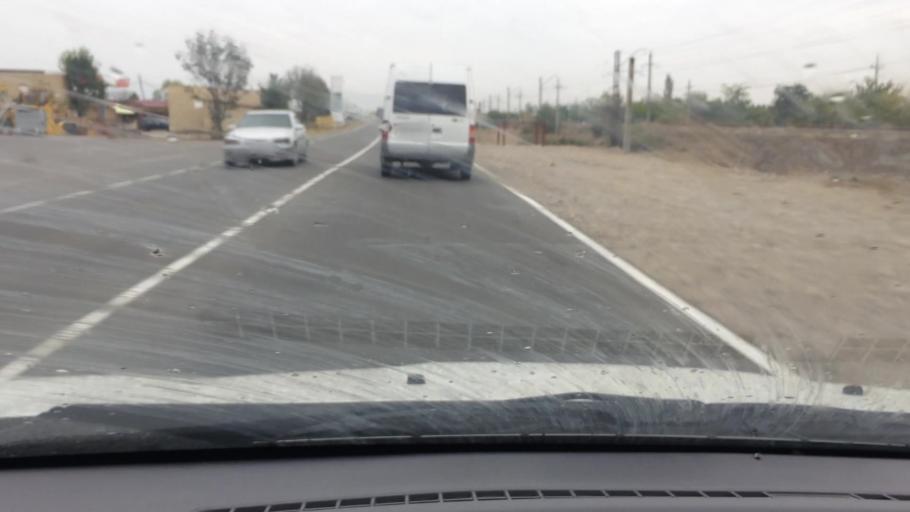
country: GE
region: Kvemo Kartli
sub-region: Marneuli
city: Marneuli
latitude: 41.4368
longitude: 44.8189
